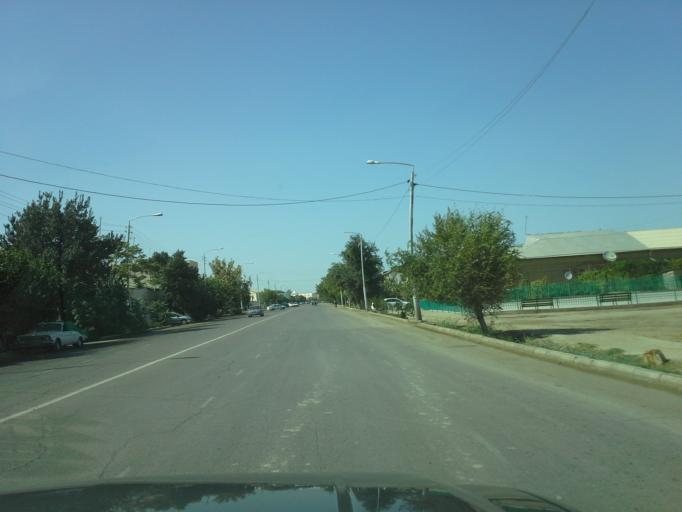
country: TM
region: Dasoguz
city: Dasoguz
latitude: 41.8184
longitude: 59.9832
